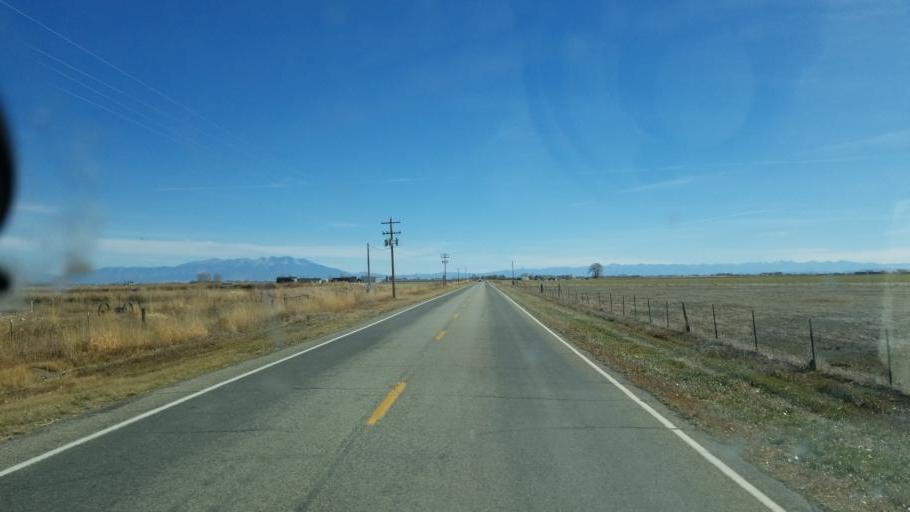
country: US
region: Colorado
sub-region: Rio Grande County
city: Monte Vista
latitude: 37.4301
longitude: -106.1119
